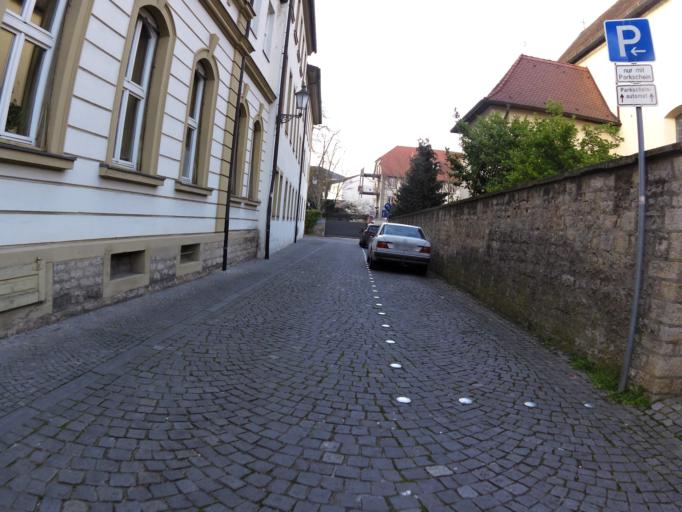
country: DE
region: Bavaria
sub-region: Regierungsbezirk Unterfranken
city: Kitzingen
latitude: 49.7358
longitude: 10.1624
